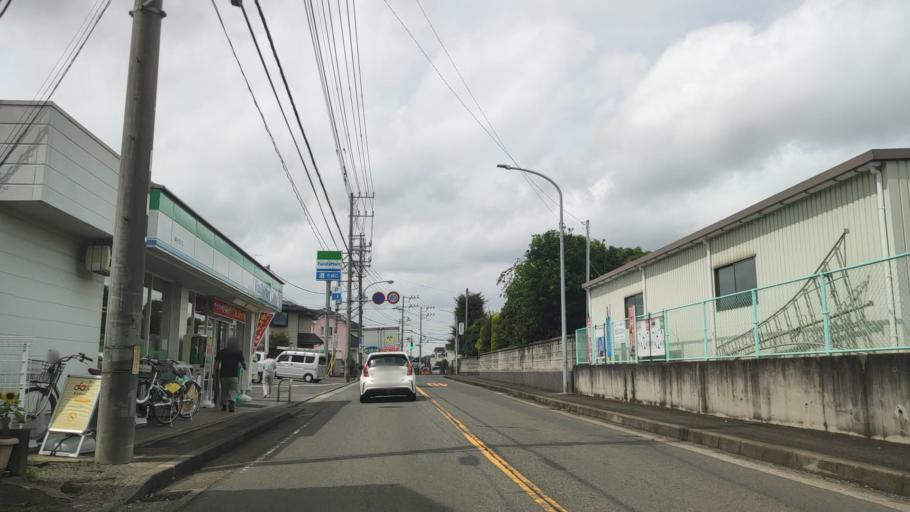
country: JP
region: Kanagawa
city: Minami-rinkan
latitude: 35.4718
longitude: 139.4897
